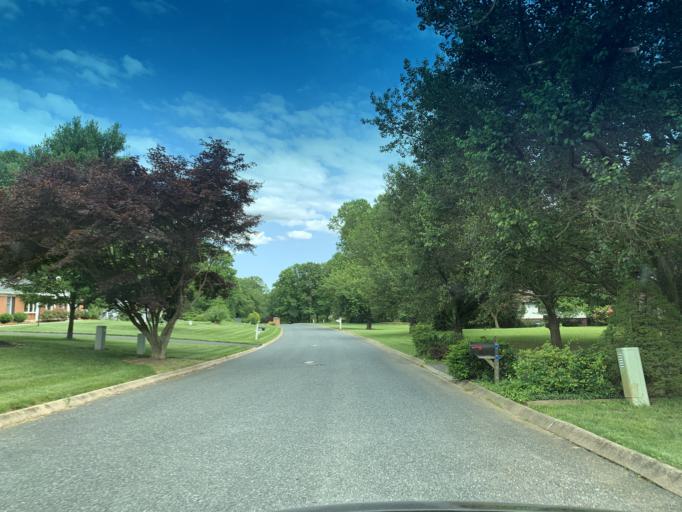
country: US
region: Maryland
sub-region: Harford County
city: Jarrettsville
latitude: 39.5973
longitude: -76.4615
